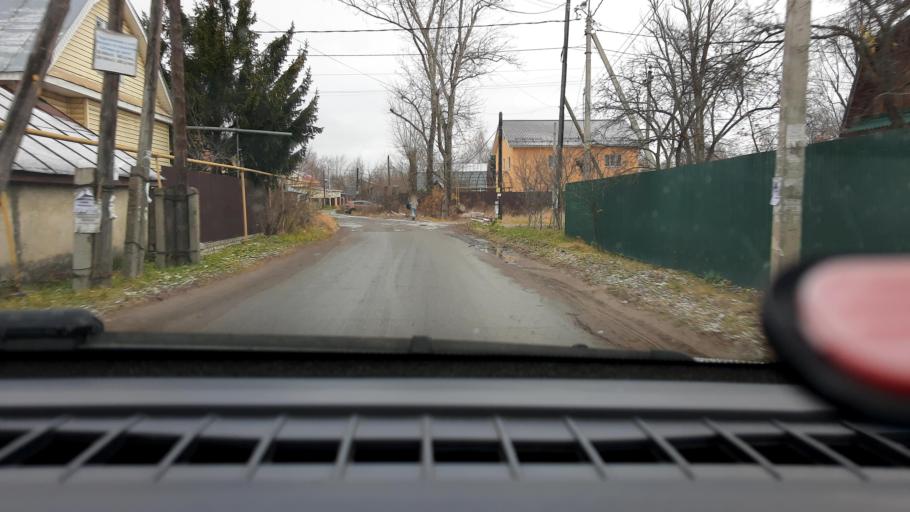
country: RU
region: Nizjnij Novgorod
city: Burevestnik
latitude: 56.2033
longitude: 43.7928
